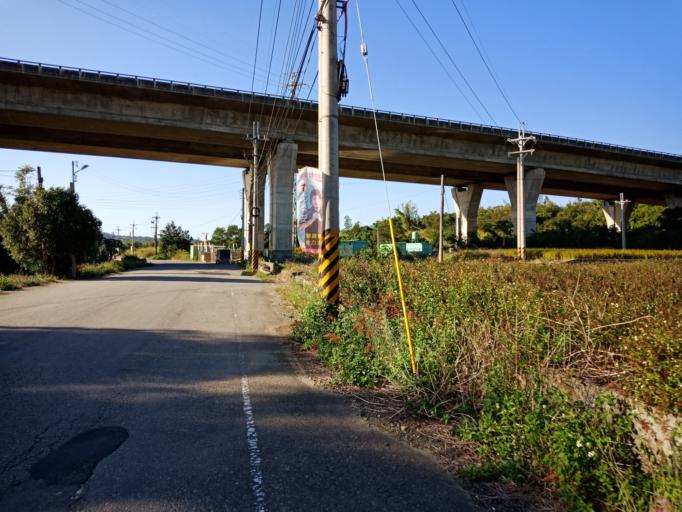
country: TW
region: Taiwan
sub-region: Miaoli
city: Miaoli
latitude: 24.4854
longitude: 120.7024
